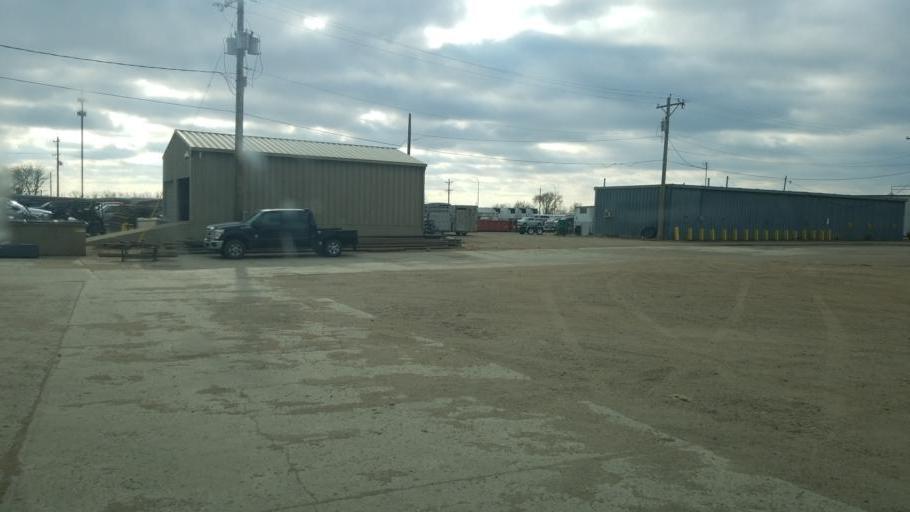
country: US
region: South Dakota
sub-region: Yankton County
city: Yankton
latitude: 42.8755
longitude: -97.3762
